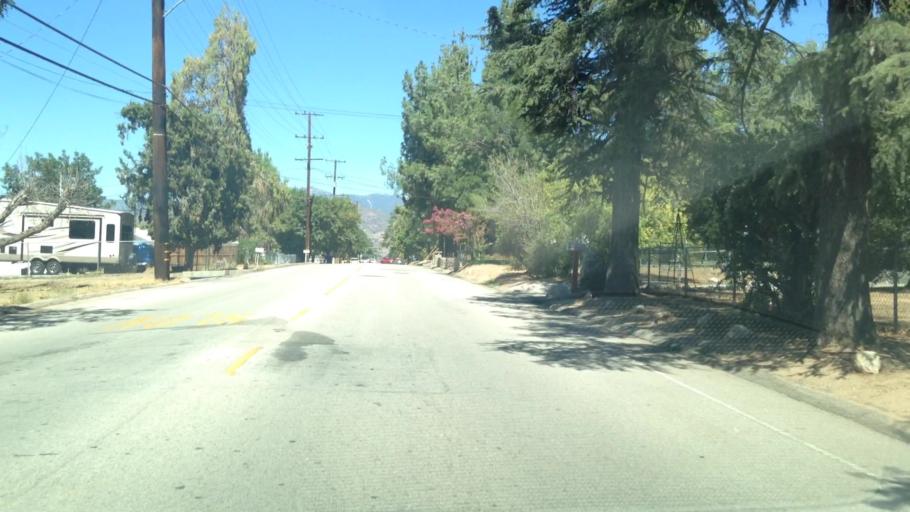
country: US
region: California
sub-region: San Bernardino County
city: Yucaipa
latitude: 34.0303
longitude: -117.0345
